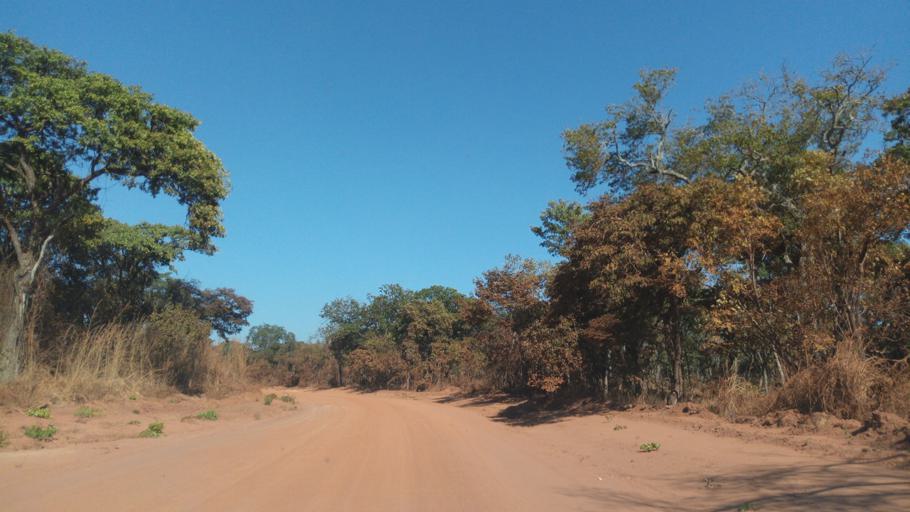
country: ZM
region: Luapula
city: Mwense
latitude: -10.7394
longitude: 28.3328
